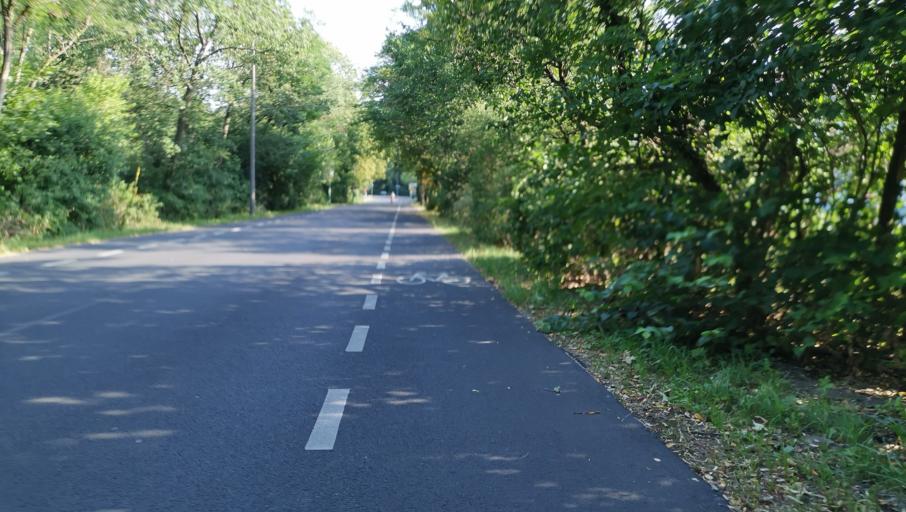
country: DE
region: Brandenburg
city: Potsdam
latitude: 52.3925
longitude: 13.0114
